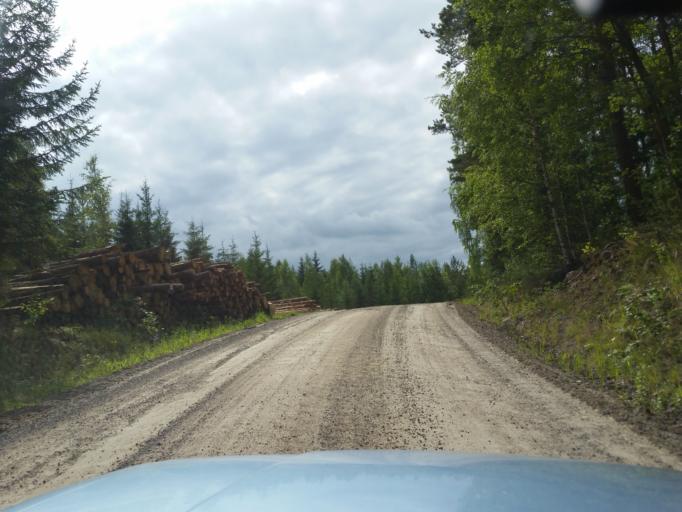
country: FI
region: Southern Savonia
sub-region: Savonlinna
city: Sulkava
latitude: 61.7350
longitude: 28.3300
